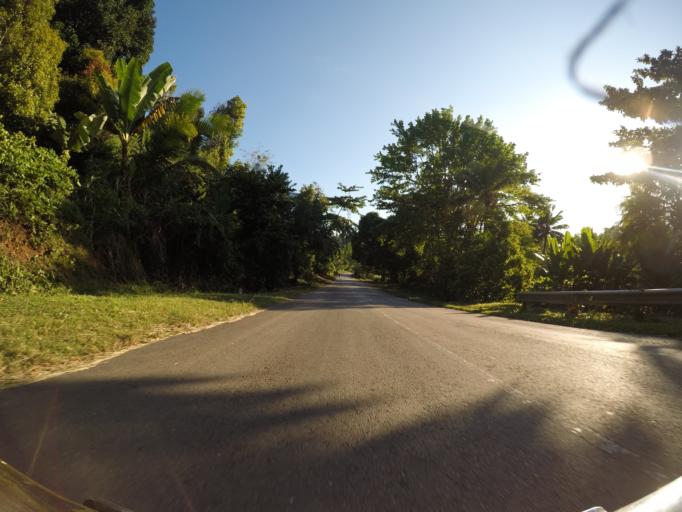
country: TZ
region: Pemba South
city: Mtambile
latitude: -5.3744
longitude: 39.6932
